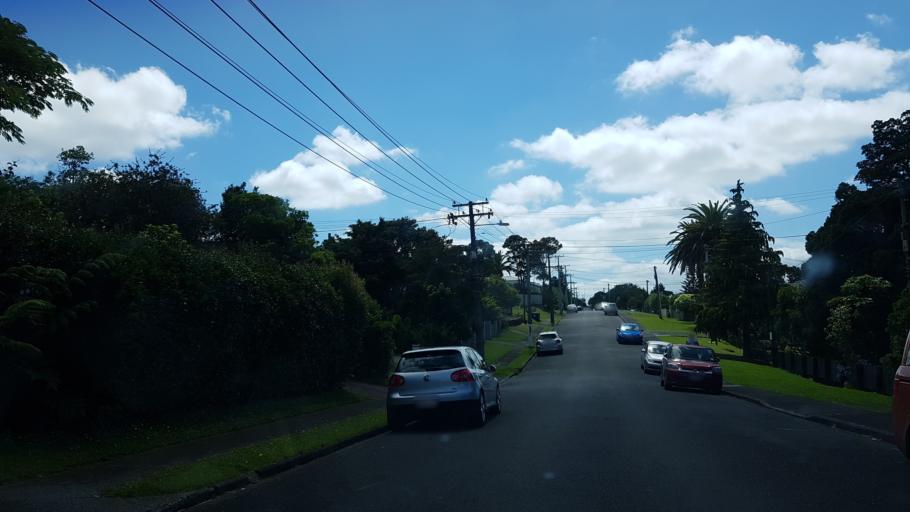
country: NZ
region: Auckland
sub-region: Auckland
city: North Shore
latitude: -36.7922
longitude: 174.7178
